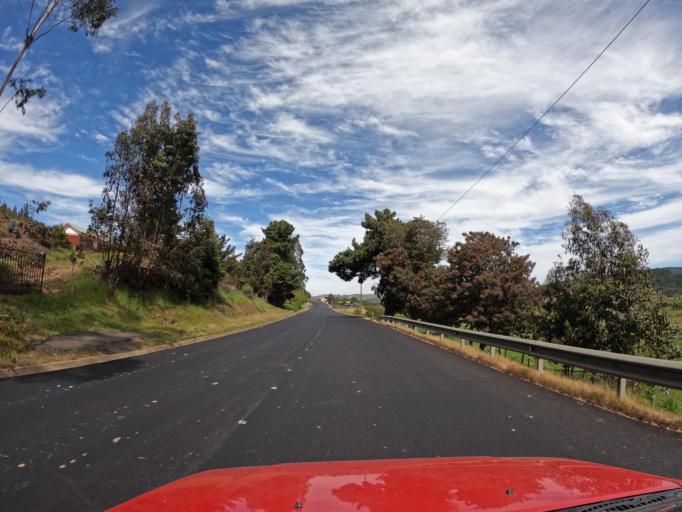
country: CL
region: Maule
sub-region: Provincia de Talca
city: Constitucion
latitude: -35.0769
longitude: -72.0378
